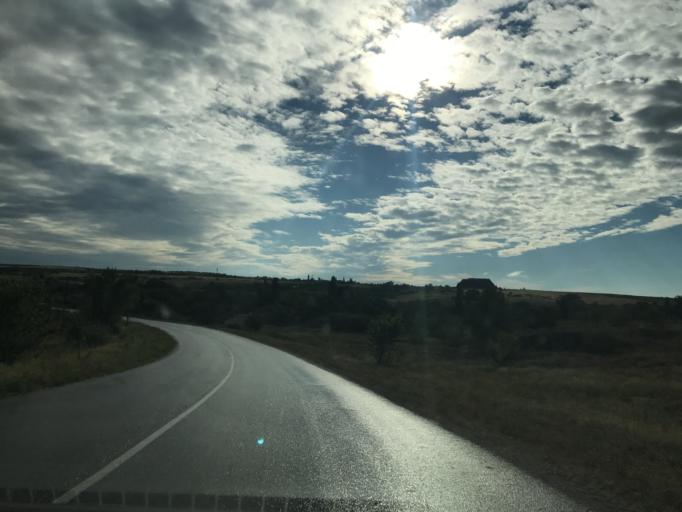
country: RU
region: Rostov
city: Likhovskoy
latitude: 48.2436
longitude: 40.1270
